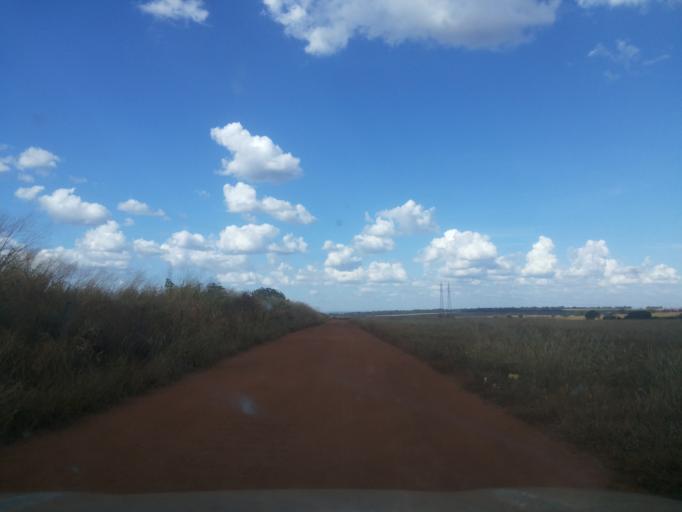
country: BR
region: Minas Gerais
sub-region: Capinopolis
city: Capinopolis
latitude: -18.5817
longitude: -49.5101
